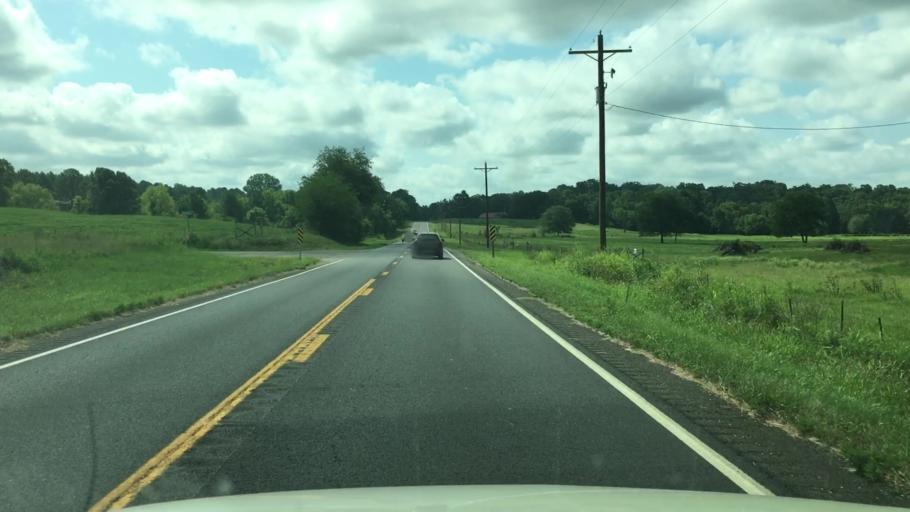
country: US
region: Arkansas
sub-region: Garland County
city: Lake Hamilton
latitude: 34.3362
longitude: -93.1792
